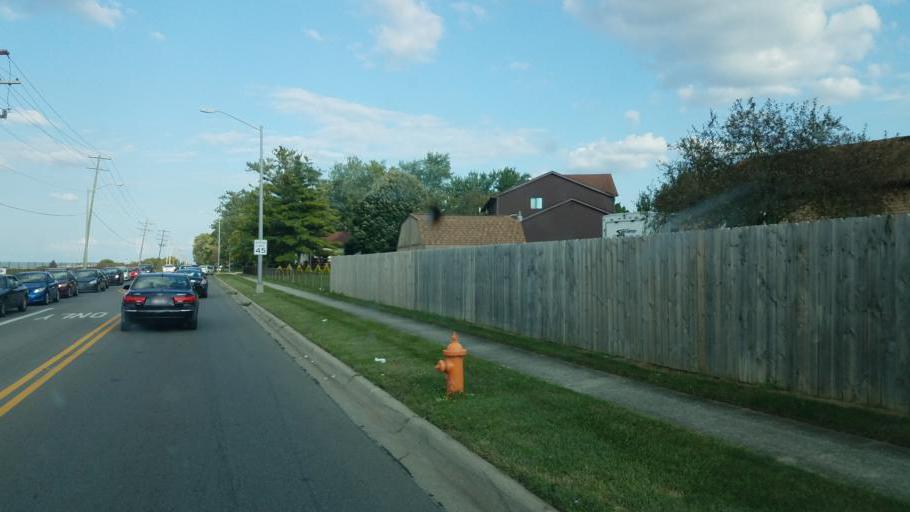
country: US
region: Ohio
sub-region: Franklin County
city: Dublin
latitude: 40.0735
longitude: -83.0924
